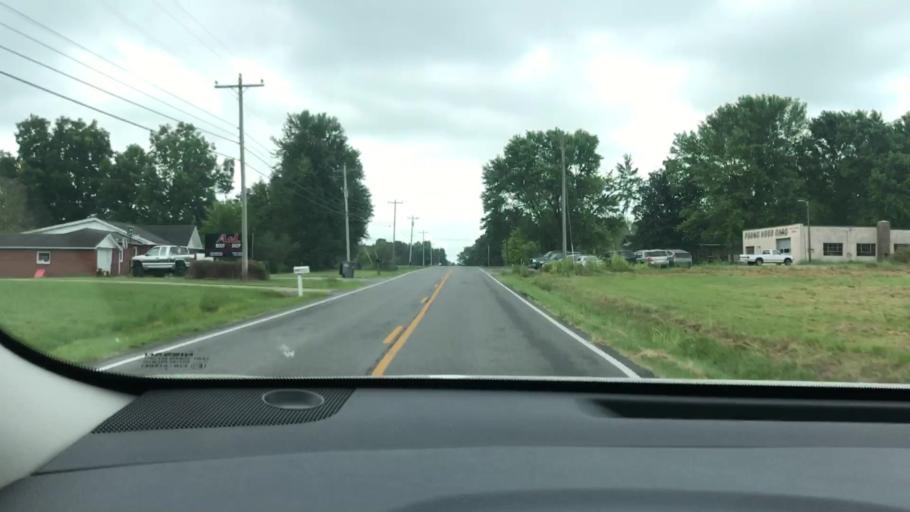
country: US
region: Kentucky
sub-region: Calloway County
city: Murray
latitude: 36.6843
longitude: -88.2993
